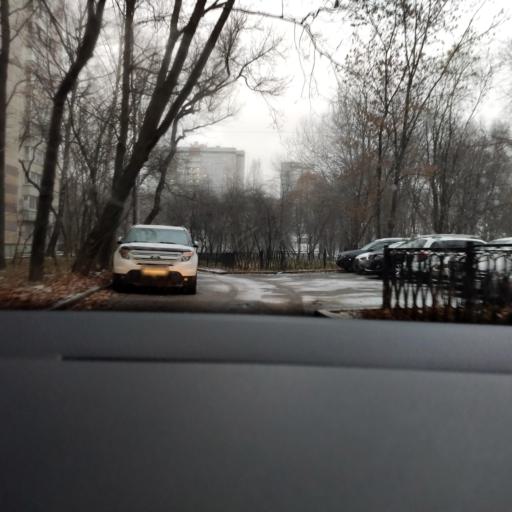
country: RU
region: Moscow
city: Leonovo
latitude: 55.8485
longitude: 37.6477
